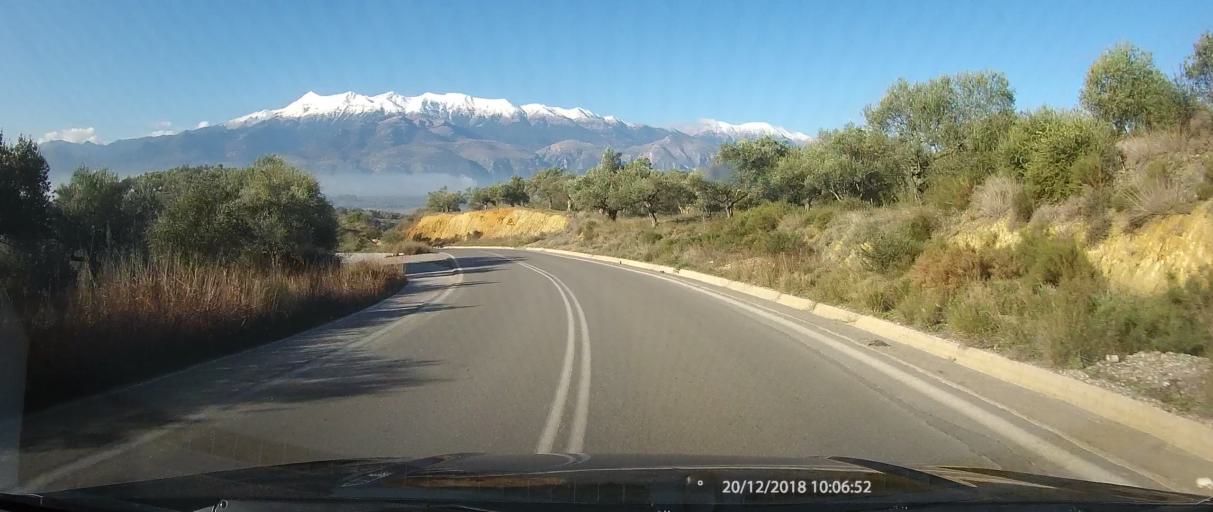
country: GR
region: Peloponnese
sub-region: Nomos Lakonias
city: Sparti
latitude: 37.0229
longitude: 22.5029
